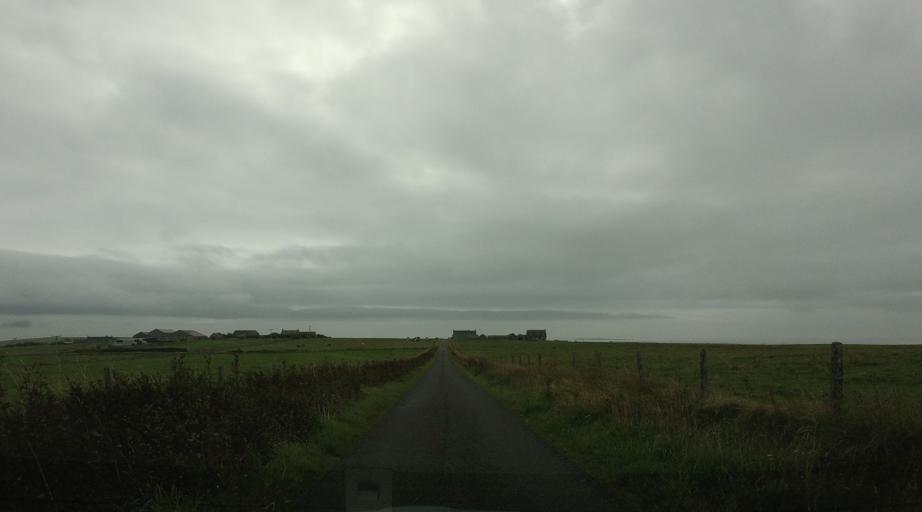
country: GB
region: Scotland
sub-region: Orkney Islands
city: Orkney
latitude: 58.7656
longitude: -2.9629
